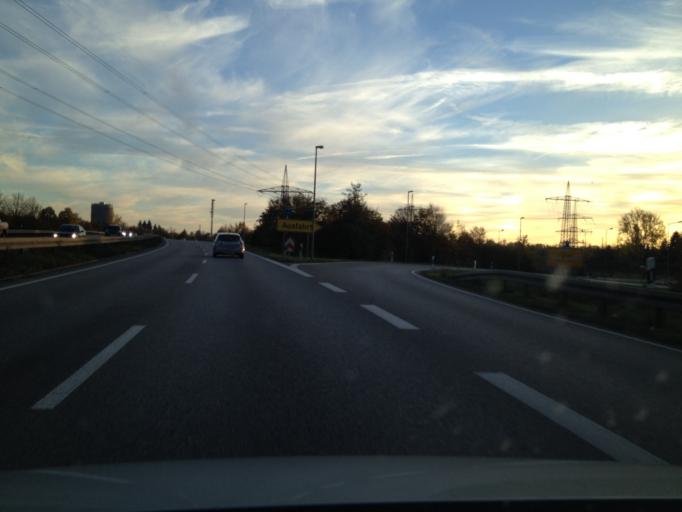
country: DE
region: Bavaria
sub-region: Swabia
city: Gersthofen
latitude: 48.4010
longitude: 10.8703
